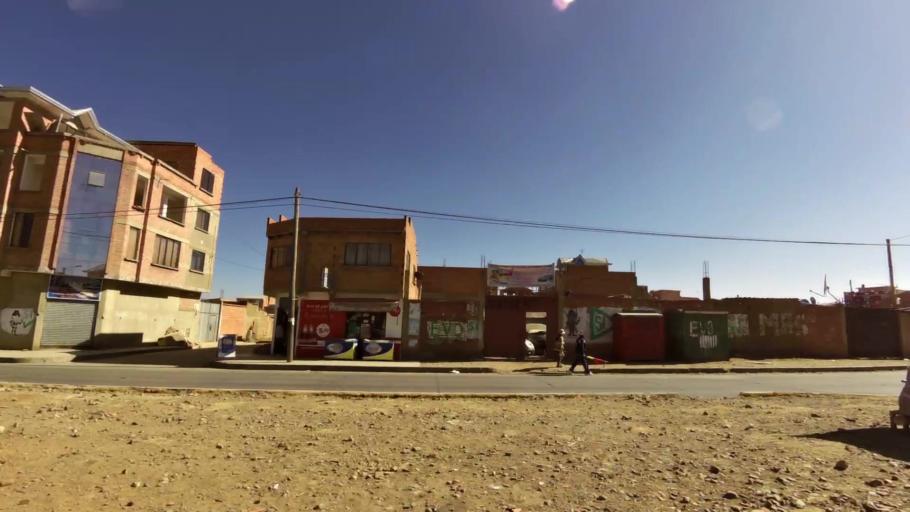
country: BO
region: La Paz
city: La Paz
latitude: -16.5296
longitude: -68.2086
